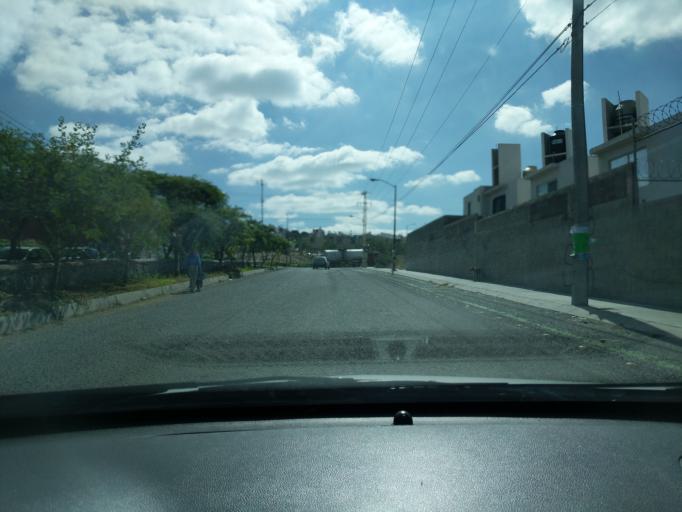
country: MX
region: Queretaro
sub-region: Queretaro
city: Patria Nueva
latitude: 20.6411
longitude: -100.4822
